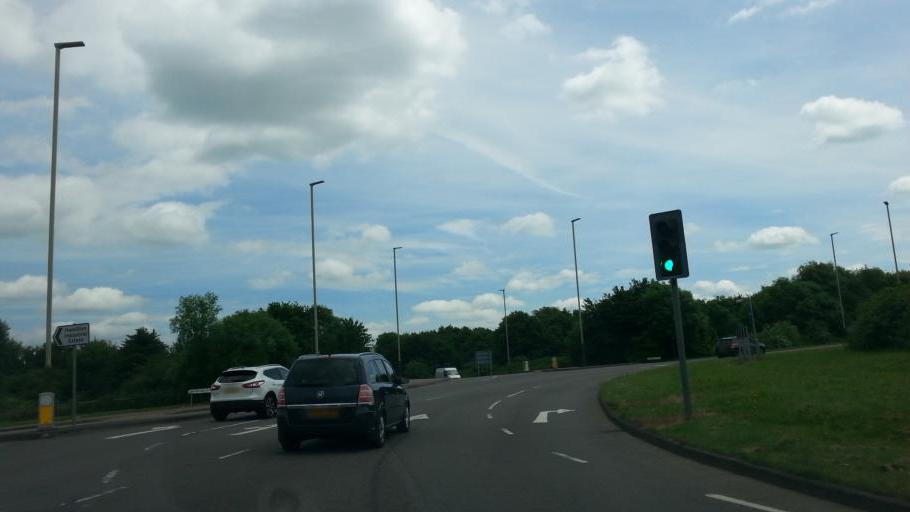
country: GB
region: England
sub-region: Leicestershire
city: Syston
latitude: 52.6579
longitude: -1.0797
